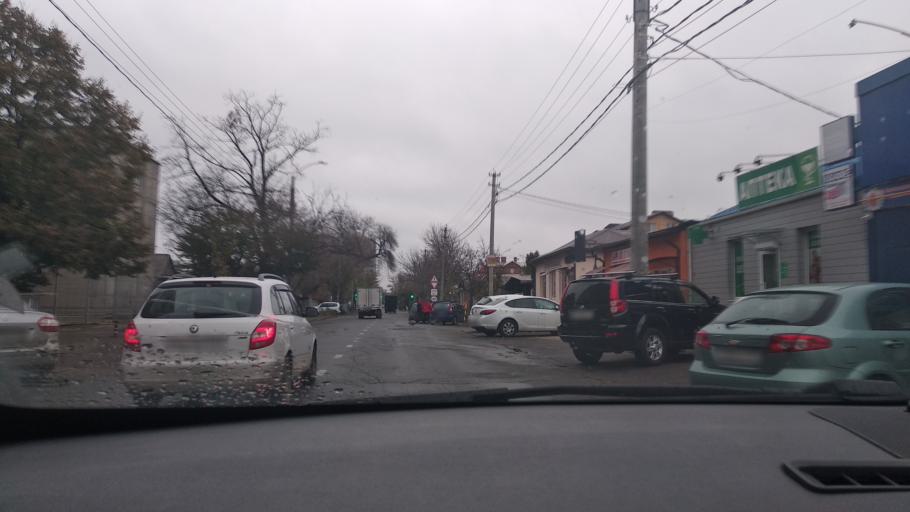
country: RU
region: Krasnodarskiy
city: Krasnodar
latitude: 45.0329
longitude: 38.9845
